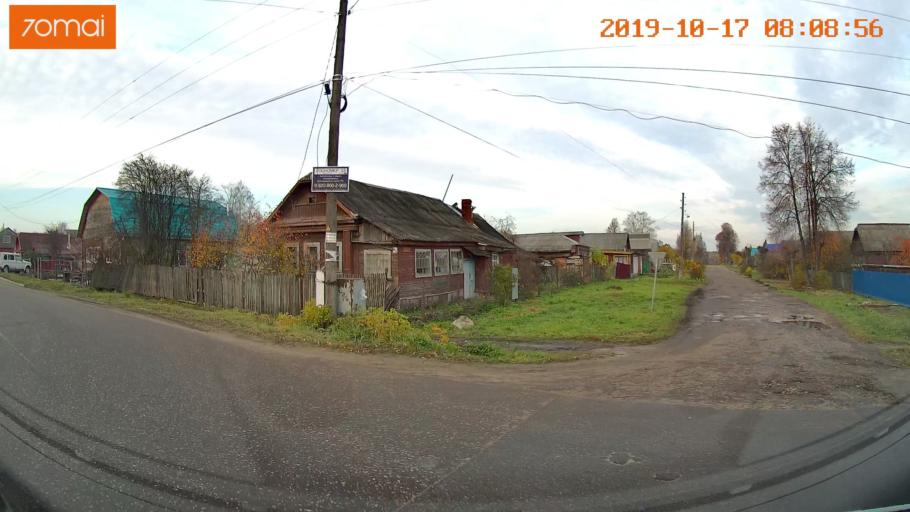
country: RU
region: Vladimir
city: Kol'chugino
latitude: 56.3149
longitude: 39.3825
